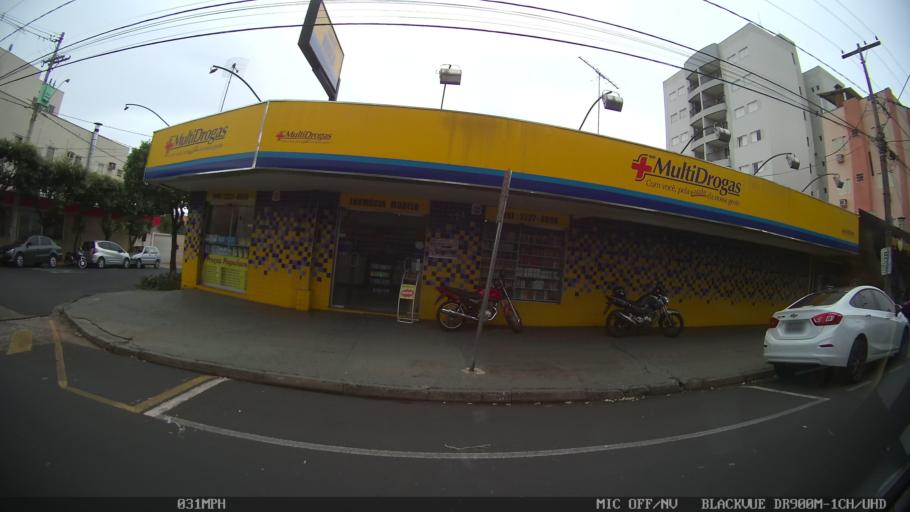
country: BR
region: Sao Paulo
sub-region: Sao Jose Do Rio Preto
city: Sao Jose do Rio Preto
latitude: -20.8375
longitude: -49.3864
